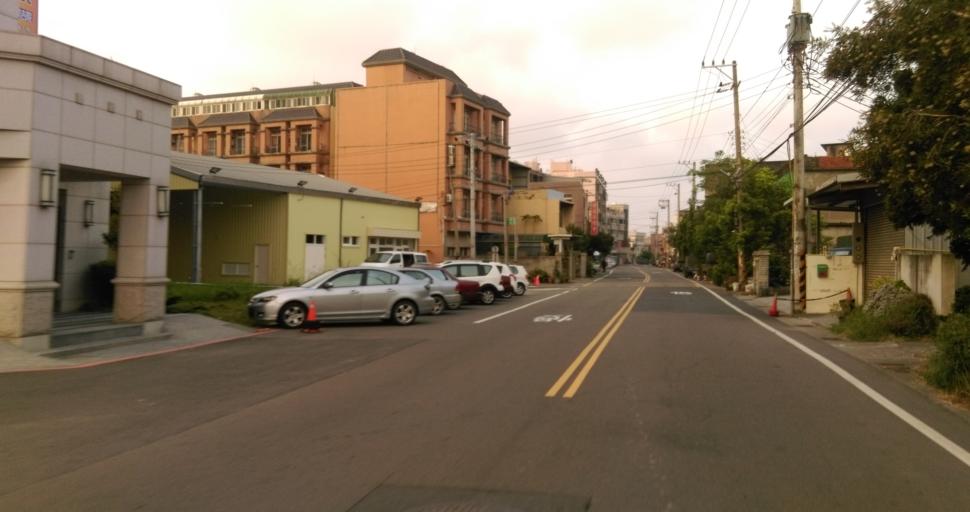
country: TW
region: Taiwan
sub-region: Hsinchu
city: Hsinchu
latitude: 24.8327
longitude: 120.9294
